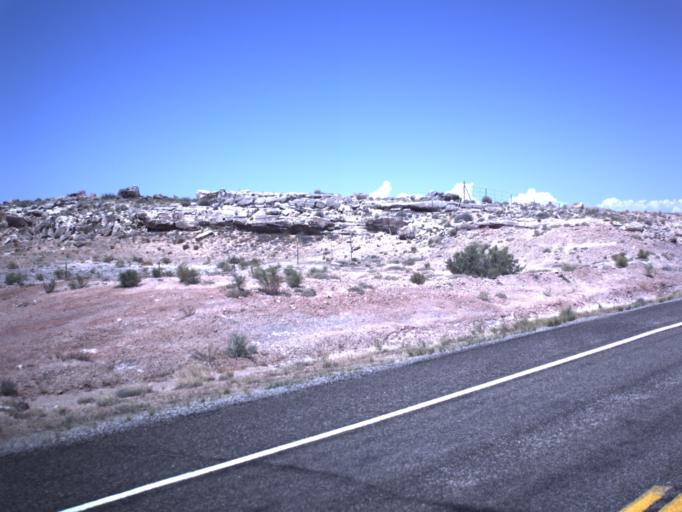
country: US
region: Utah
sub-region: Carbon County
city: East Carbon City
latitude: 38.9046
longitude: -110.3667
